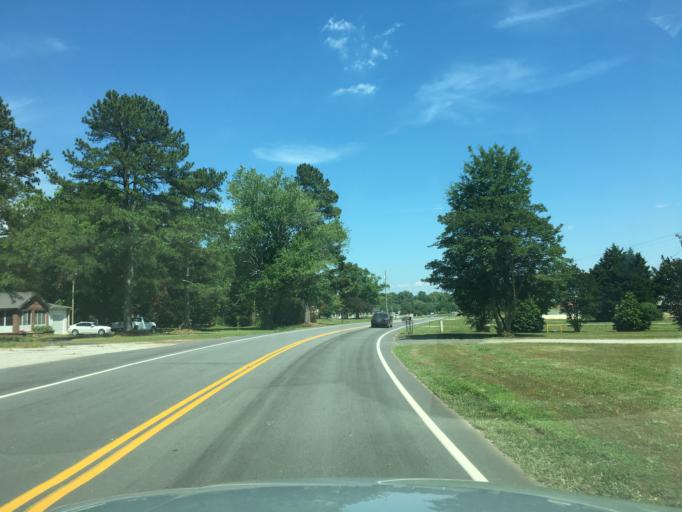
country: US
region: Georgia
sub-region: Hart County
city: Reed Creek
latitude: 34.5126
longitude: -82.9822
